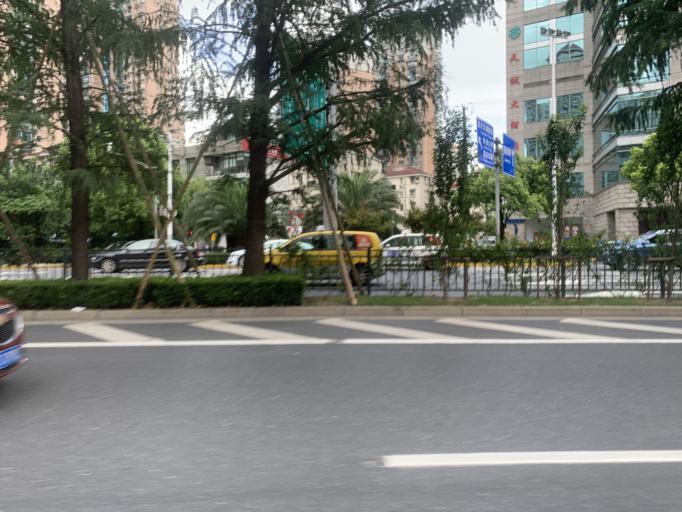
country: CN
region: Shanghai Shi
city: Luwan
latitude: 31.2079
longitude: 121.4665
